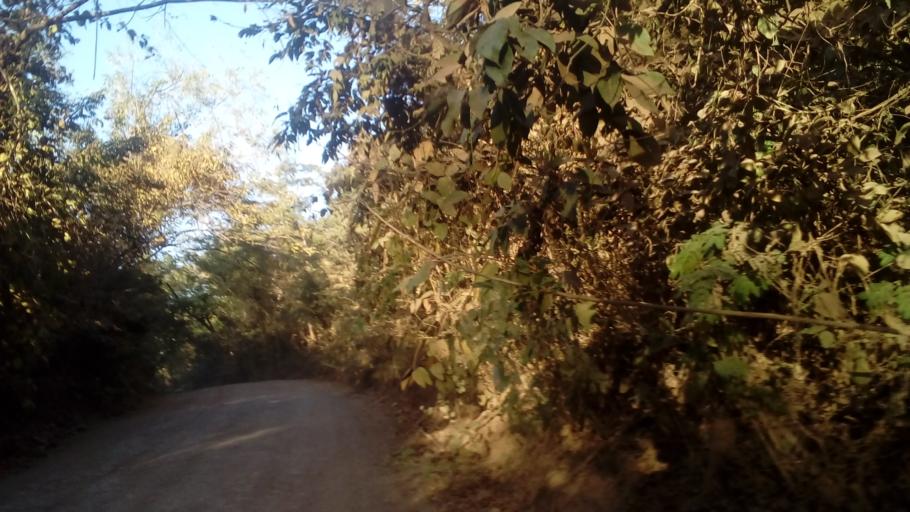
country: CR
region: Guanacaste
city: Sardinal
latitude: 10.3912
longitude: -85.8232
